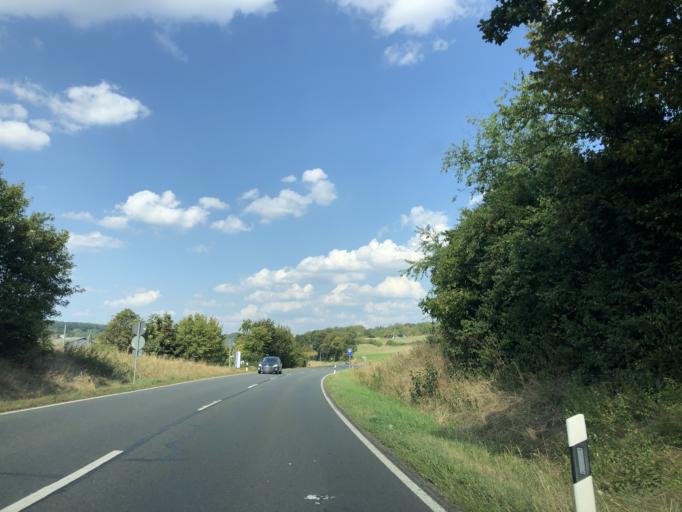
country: DE
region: Hesse
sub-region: Regierungsbezirk Giessen
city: Kirchhain
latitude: 50.8335
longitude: 8.9208
